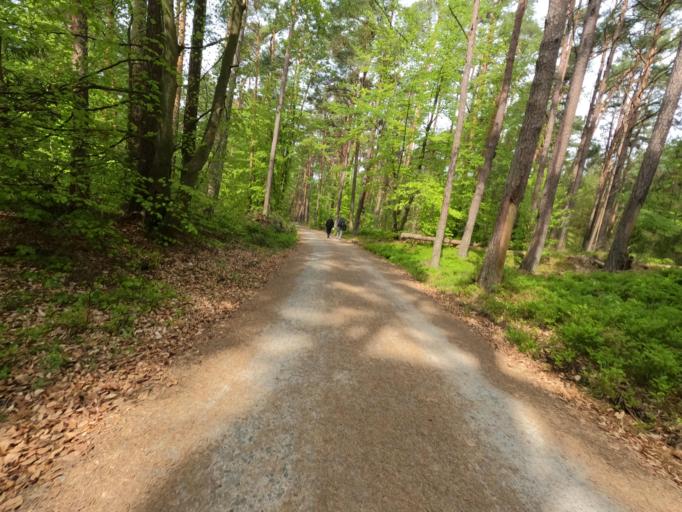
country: DE
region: Mecklenburg-Vorpommern
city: Ostseebad Prerow
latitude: 54.4505
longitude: 12.5216
